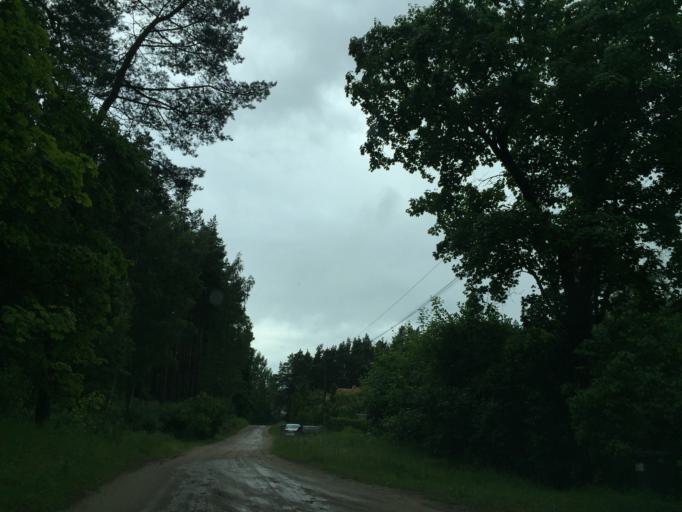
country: LV
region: Riga
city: Jaunciems
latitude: 57.0535
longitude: 24.1740
